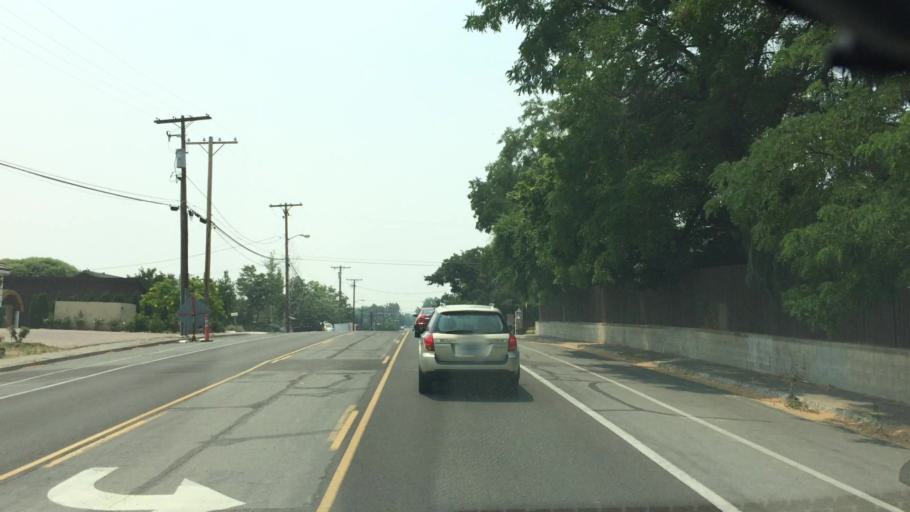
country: US
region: Nevada
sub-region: Washoe County
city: Reno
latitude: 39.5081
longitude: -119.8173
